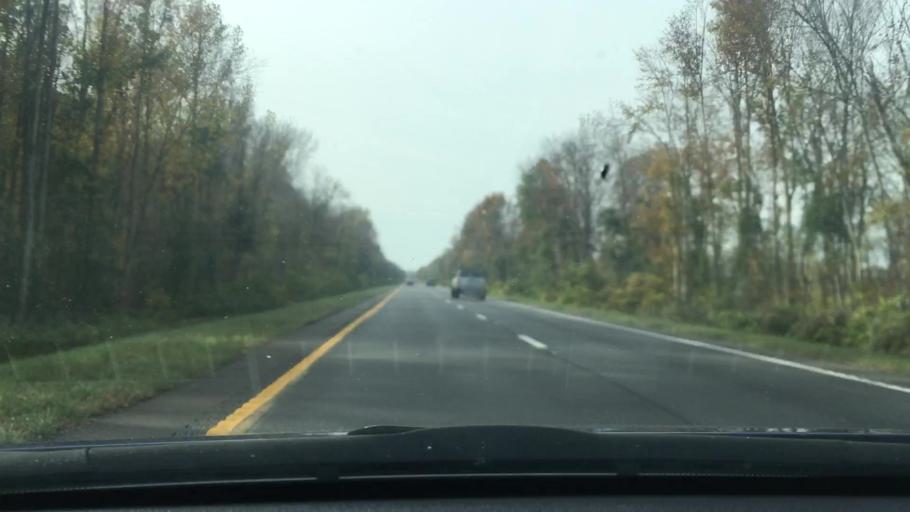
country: US
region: South Carolina
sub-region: Sumter County
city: Stateburg
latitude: 33.9509
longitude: -80.5960
